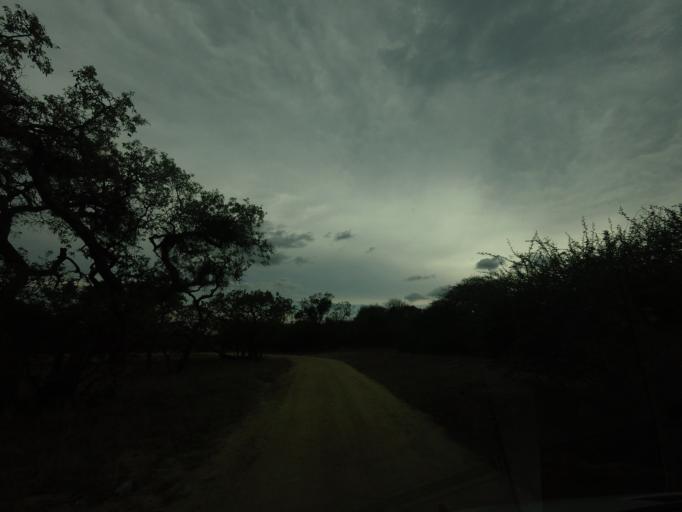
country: ZA
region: Limpopo
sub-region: Mopani District Municipality
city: Hoedspruit
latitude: -24.5132
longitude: 30.9053
